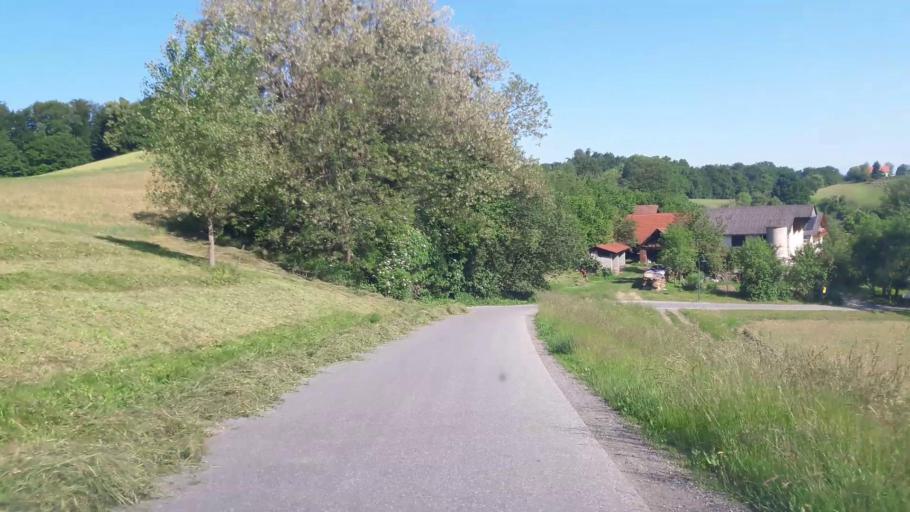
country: AT
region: Styria
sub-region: Politischer Bezirk Hartberg-Fuerstenfeld
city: UEbersbach
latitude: 47.0028
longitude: 16.0466
